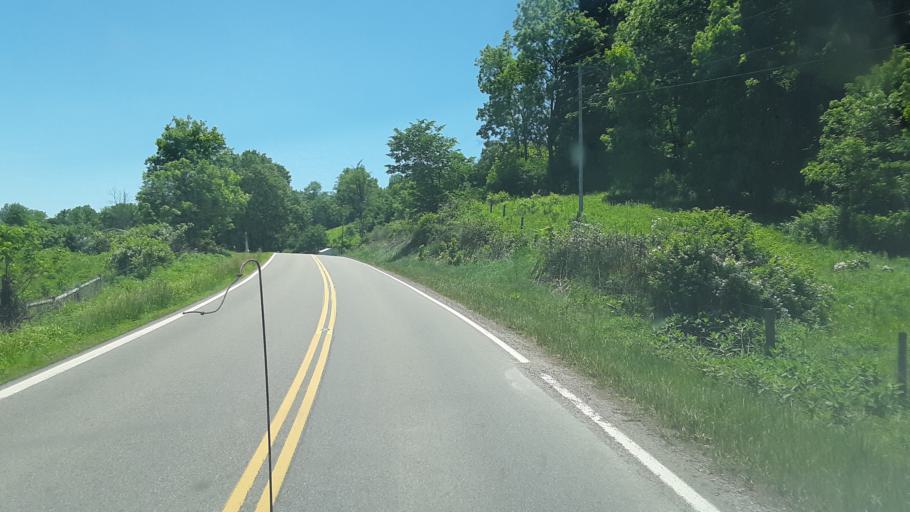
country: US
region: Ohio
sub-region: Coshocton County
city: Coshocton
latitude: 40.3205
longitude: -82.0170
